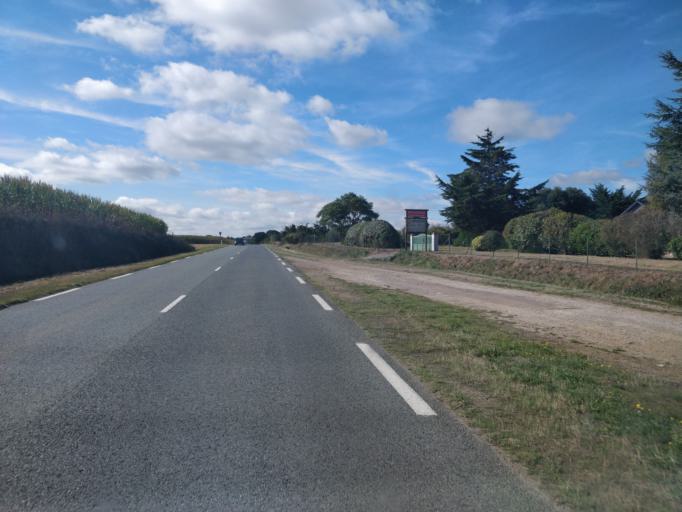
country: FR
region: Brittany
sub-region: Departement des Cotes-d'Armor
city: Erquy
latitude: 48.6087
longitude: -2.4671
